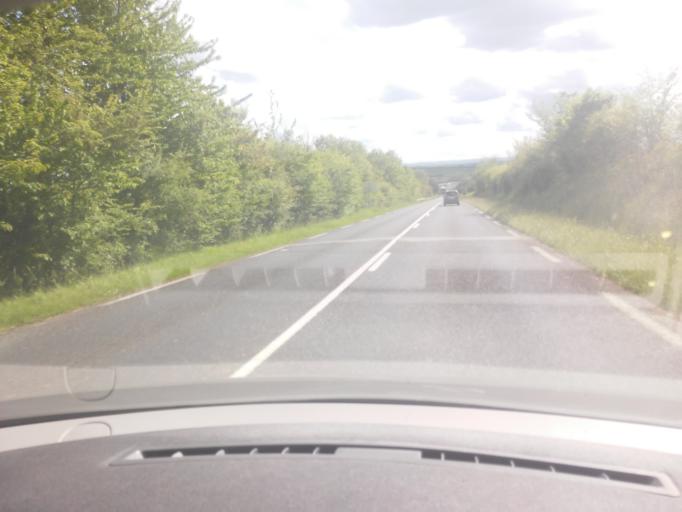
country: FR
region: Lorraine
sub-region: Departement de Meurthe-et-Moselle
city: Valleroy
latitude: 49.2083
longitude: 5.9159
